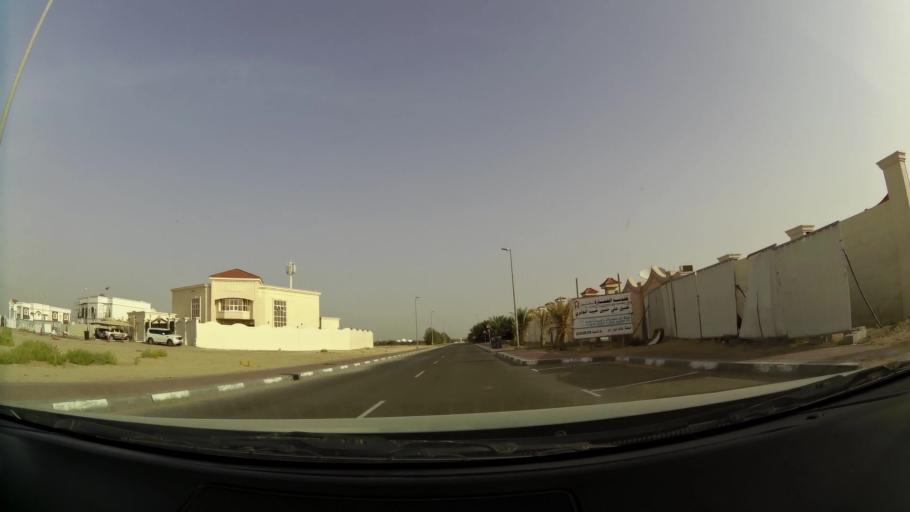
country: AE
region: Abu Dhabi
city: Al Ain
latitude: 24.1182
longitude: 55.6924
